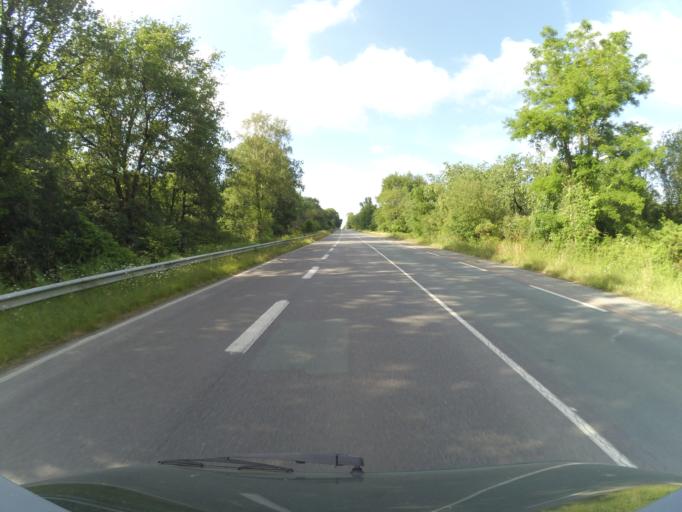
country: FR
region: Poitou-Charentes
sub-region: Departement de la Charente-Maritime
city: Le Gua
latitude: 45.7742
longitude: -0.9363
